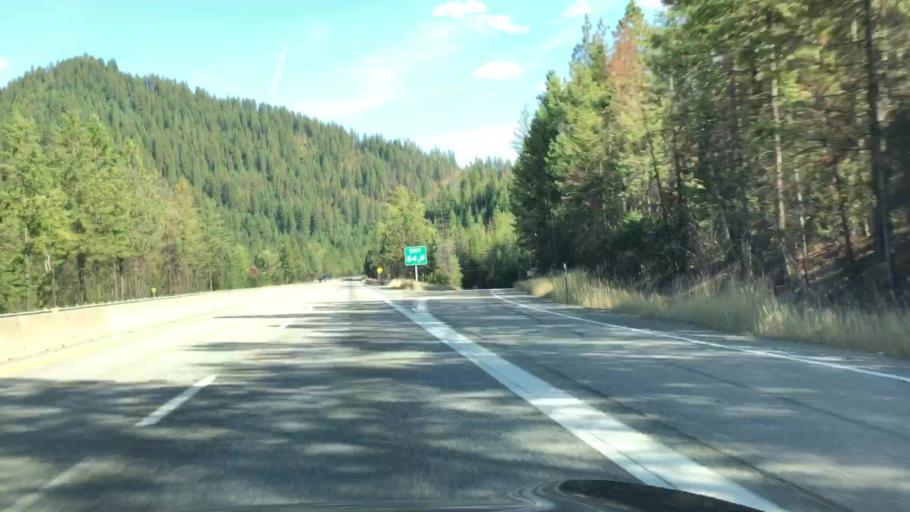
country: US
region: Idaho
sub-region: Shoshone County
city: Wallace
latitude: 47.4741
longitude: -115.8722
